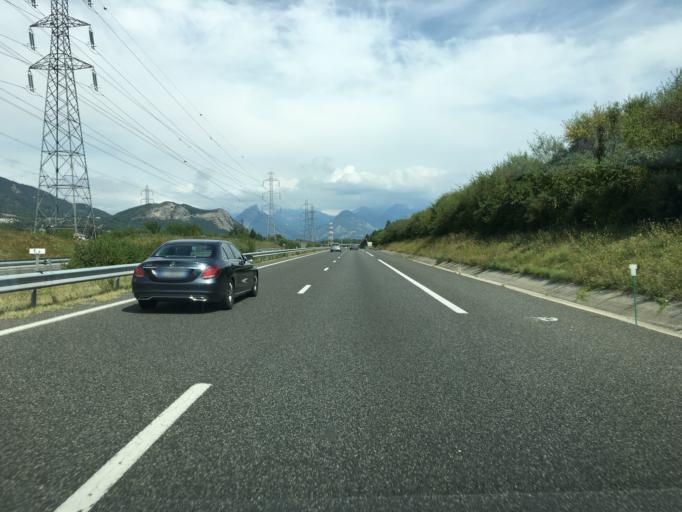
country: FR
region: Rhone-Alpes
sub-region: Departement de l'Isere
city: Allieres-et-Risset
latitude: 45.1023
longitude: 5.6761
